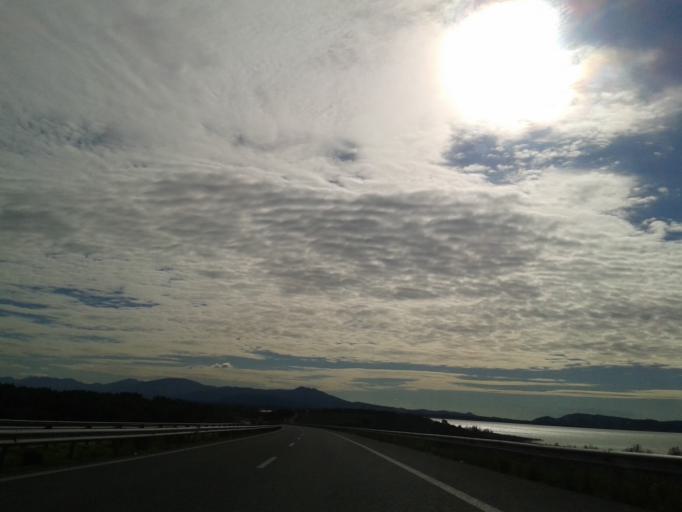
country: GR
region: West Greece
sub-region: Nomos Aitolias kai Akarnanias
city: Fitiai
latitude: 38.6813
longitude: 21.2187
